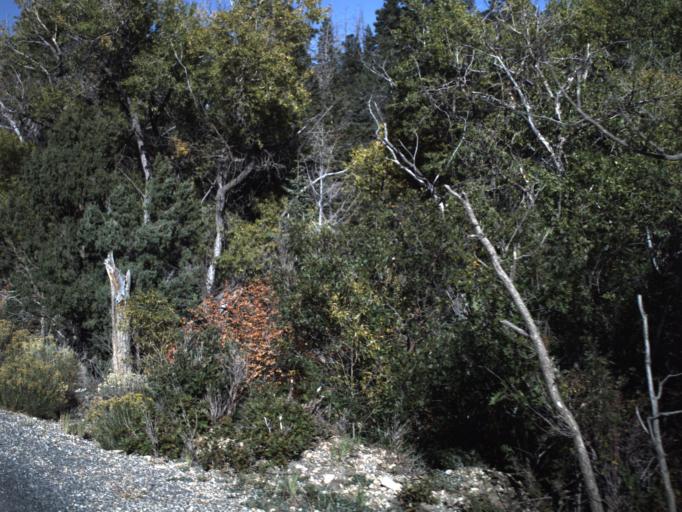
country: US
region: Utah
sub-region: Iron County
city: Parowan
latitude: 37.7647
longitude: -112.8502
